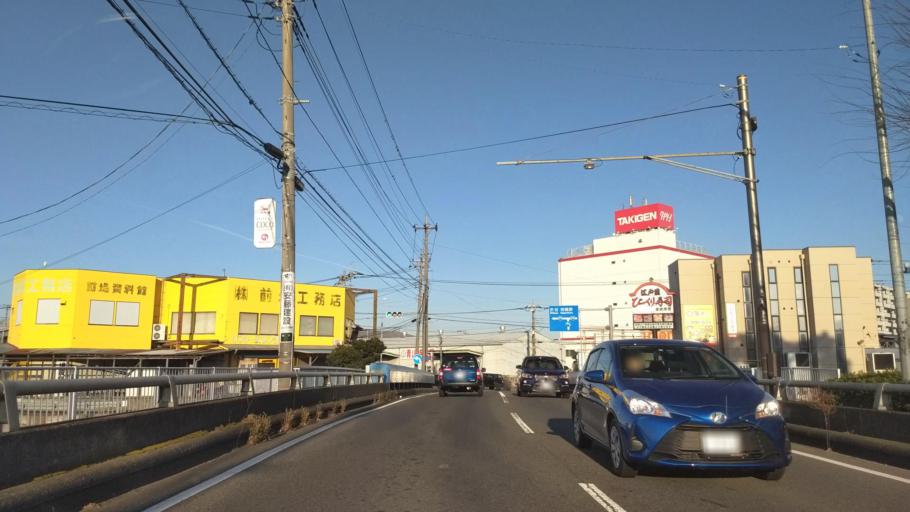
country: JP
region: Kanagawa
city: Atsugi
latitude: 35.4271
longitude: 139.3565
